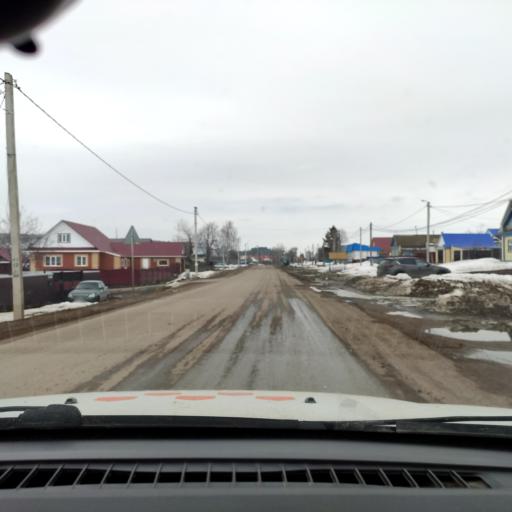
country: RU
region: Bashkortostan
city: Kushnarenkovo
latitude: 55.1093
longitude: 55.3386
